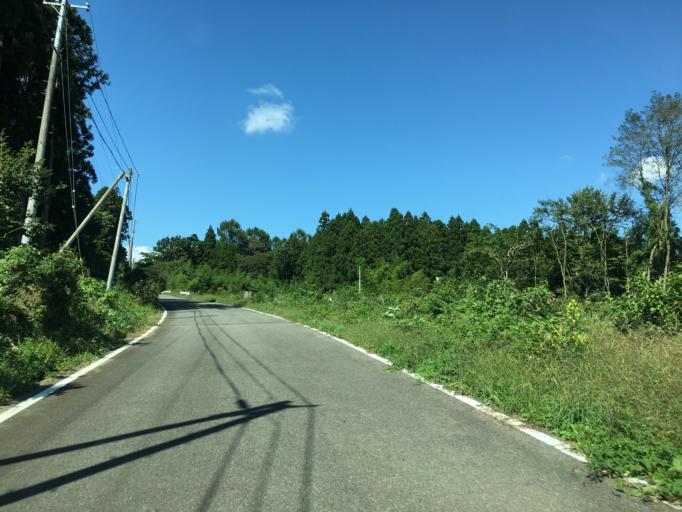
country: JP
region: Fukushima
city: Ishikawa
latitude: 37.2655
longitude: 140.5507
